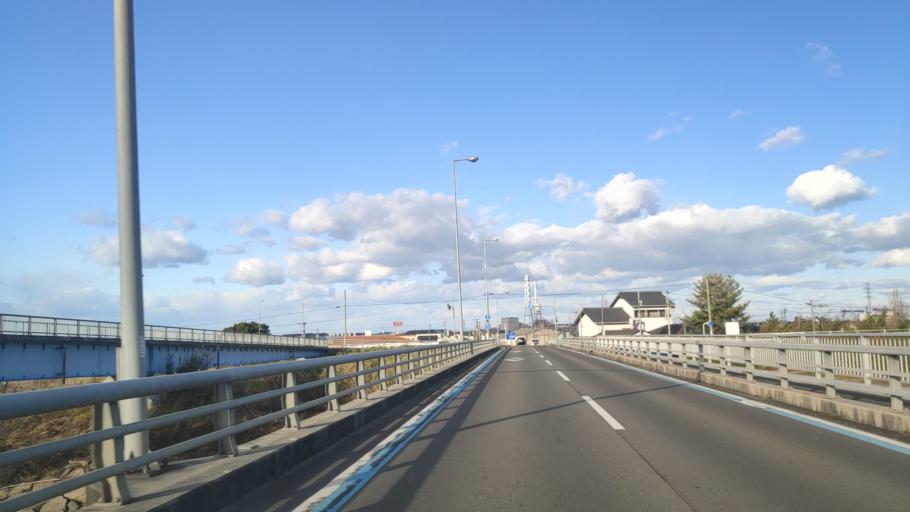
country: JP
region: Ehime
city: Saijo
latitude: 33.9129
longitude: 133.1617
